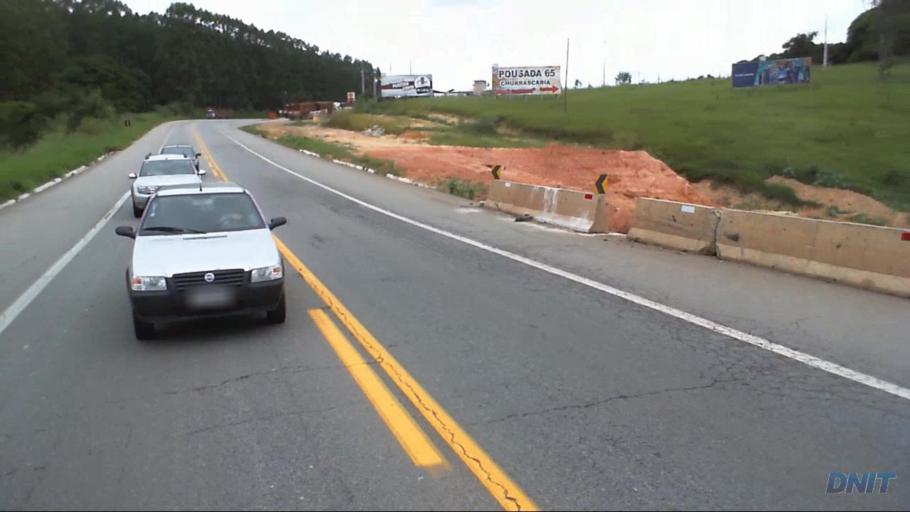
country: BR
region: Minas Gerais
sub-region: Barao De Cocais
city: Barao de Cocais
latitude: -19.7455
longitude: -43.4950
